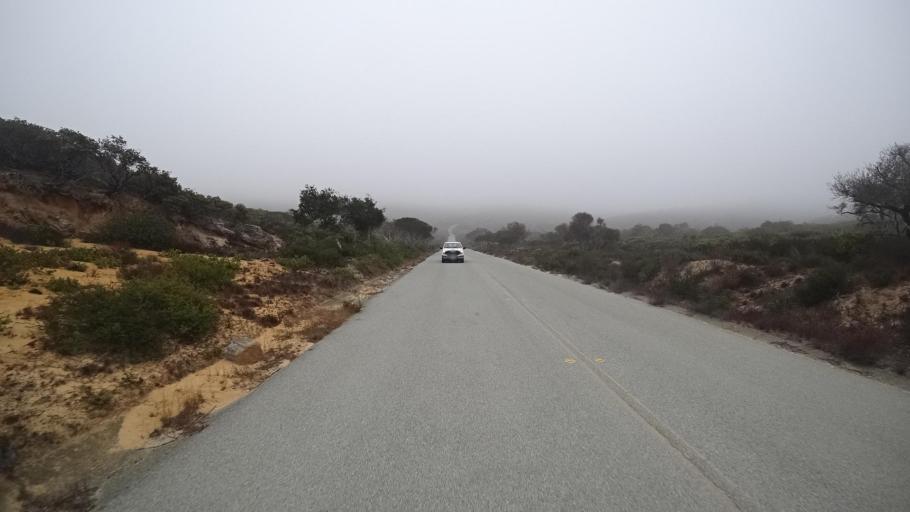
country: US
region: California
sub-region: Monterey County
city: Marina
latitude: 36.6289
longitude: -121.7396
